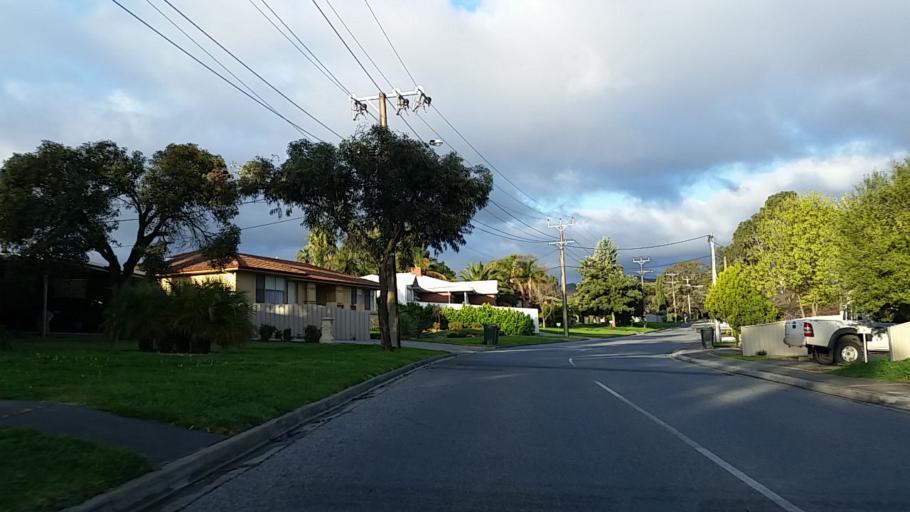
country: AU
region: South Australia
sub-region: Tea Tree Gully
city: Hope Valley
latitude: -34.8476
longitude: 138.7023
